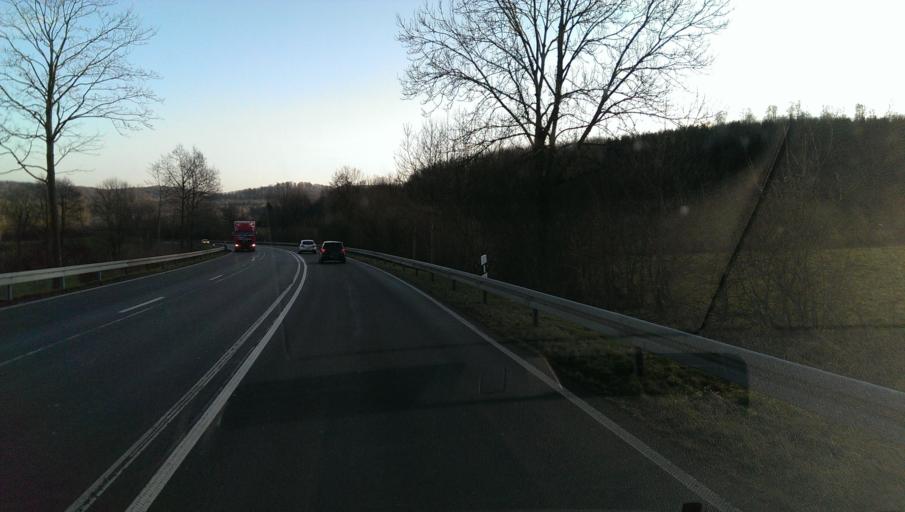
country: DE
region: North Rhine-Westphalia
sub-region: Regierungsbezirk Detmold
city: Bad Driburg
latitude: 51.7210
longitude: 9.0038
